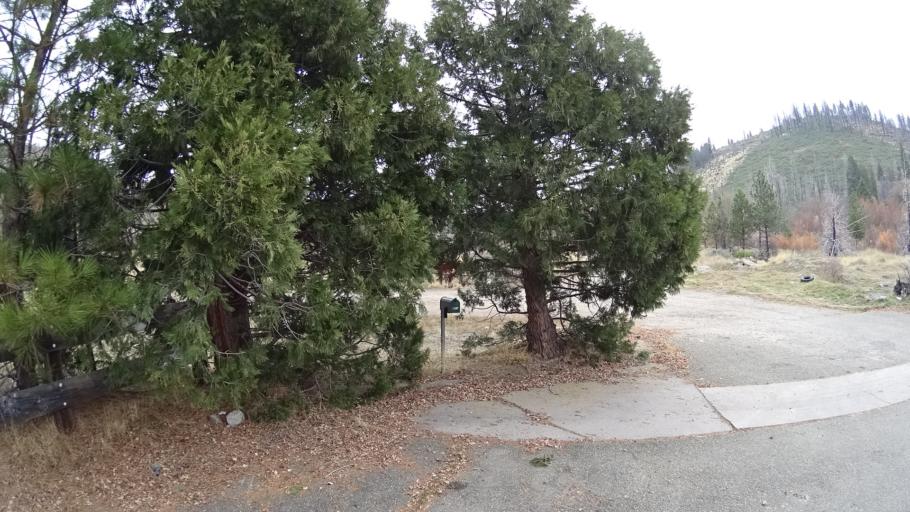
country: US
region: California
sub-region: Siskiyou County
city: Weed
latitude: 41.4220
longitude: -122.3792
